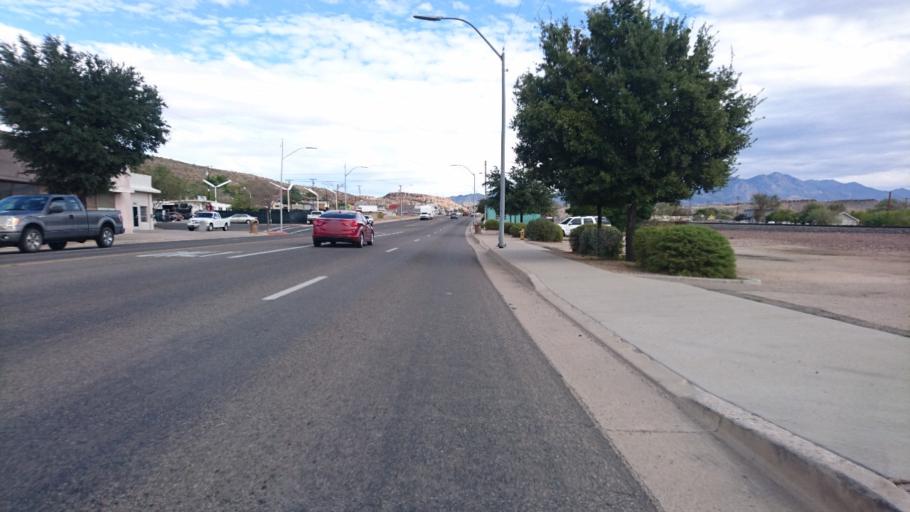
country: US
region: Arizona
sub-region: Mohave County
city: Kingman
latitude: 35.1882
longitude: -114.0501
